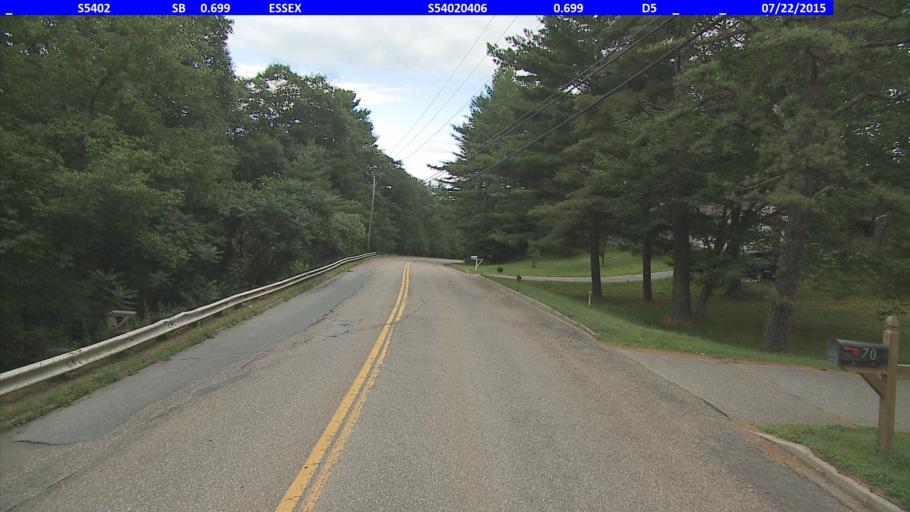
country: US
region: Vermont
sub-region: Chittenden County
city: Williston
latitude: 44.4886
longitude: -73.0500
